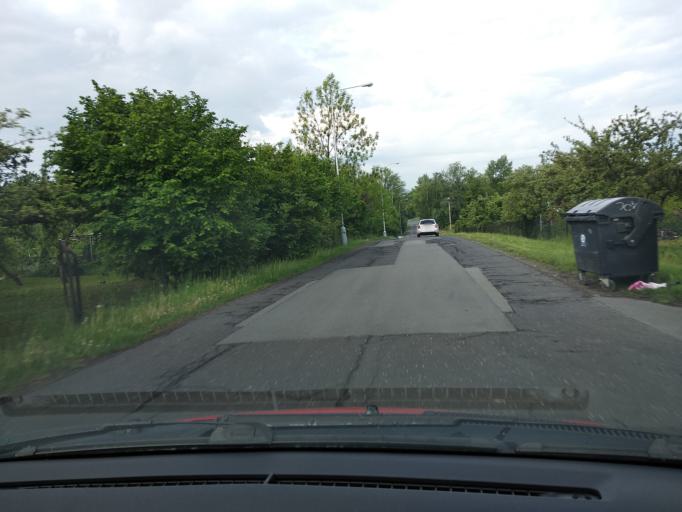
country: CZ
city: Sviadnov
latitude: 49.7005
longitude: 18.3409
